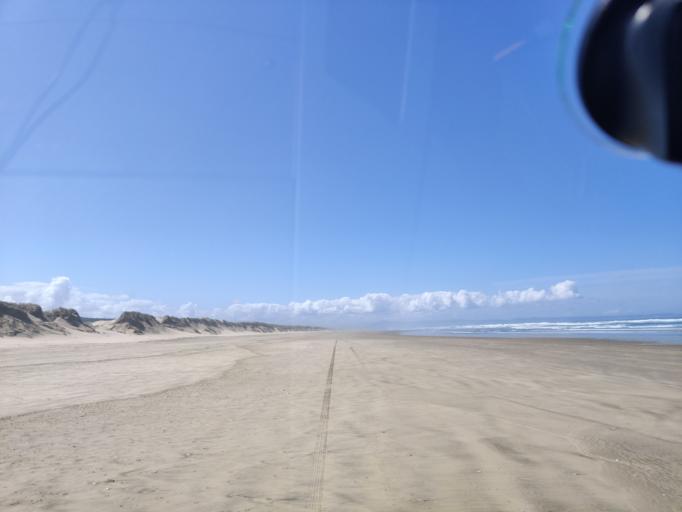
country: NZ
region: Northland
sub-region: Far North District
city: Kaitaia
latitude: -34.9399
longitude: 173.1145
